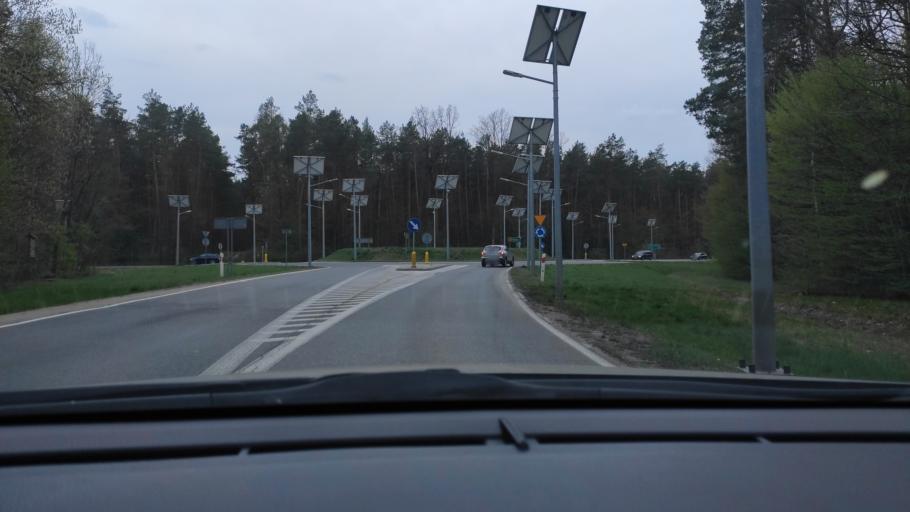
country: PL
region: Masovian Voivodeship
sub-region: Powiat radomski
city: Pionki
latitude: 51.4927
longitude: 21.4227
